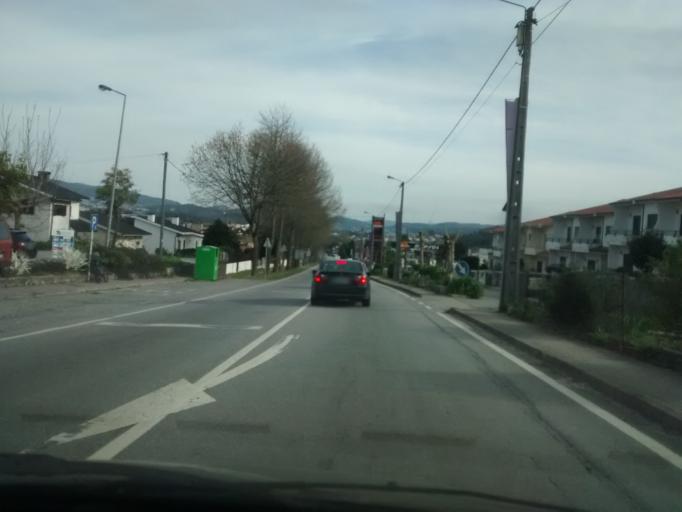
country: PT
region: Braga
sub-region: Guimaraes
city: Brito
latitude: 41.4952
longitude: -8.3625
